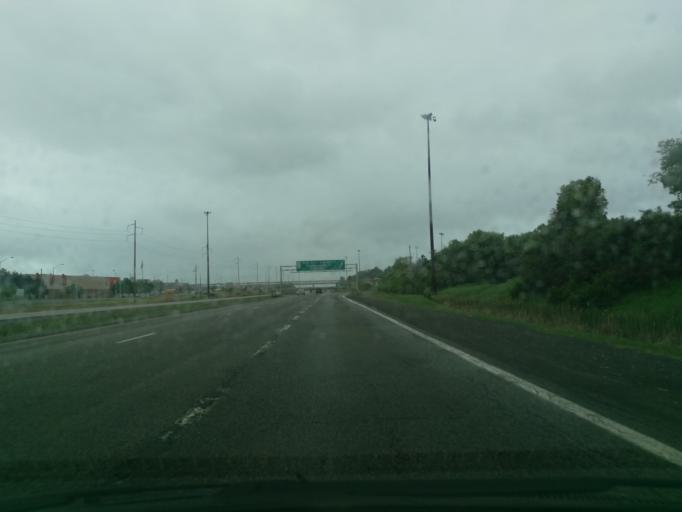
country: CA
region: Quebec
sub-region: Outaouais
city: Gatineau
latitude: 45.4824
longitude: -75.5119
